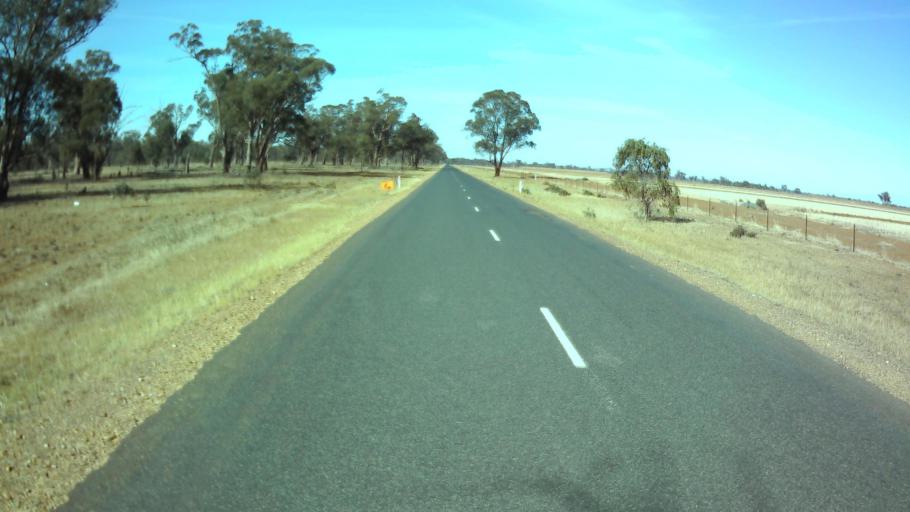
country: AU
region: New South Wales
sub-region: Weddin
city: Grenfell
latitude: -34.1191
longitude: 147.8142
